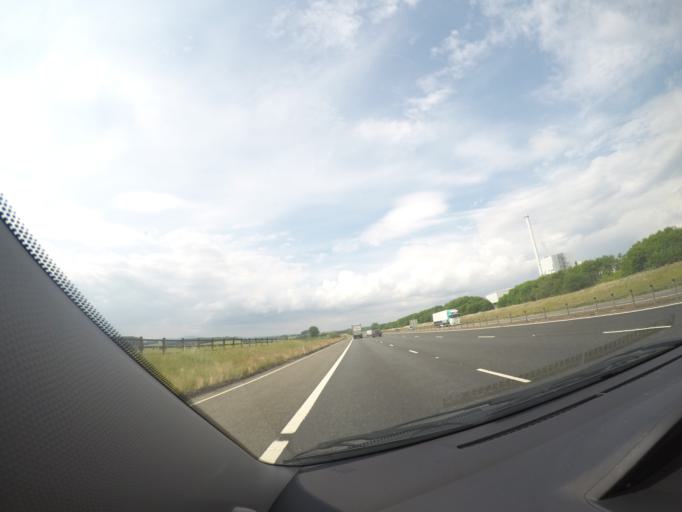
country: GB
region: Scotland
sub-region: Dumfries and Galloway
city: Lockerbie
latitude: 55.1502
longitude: -3.3827
